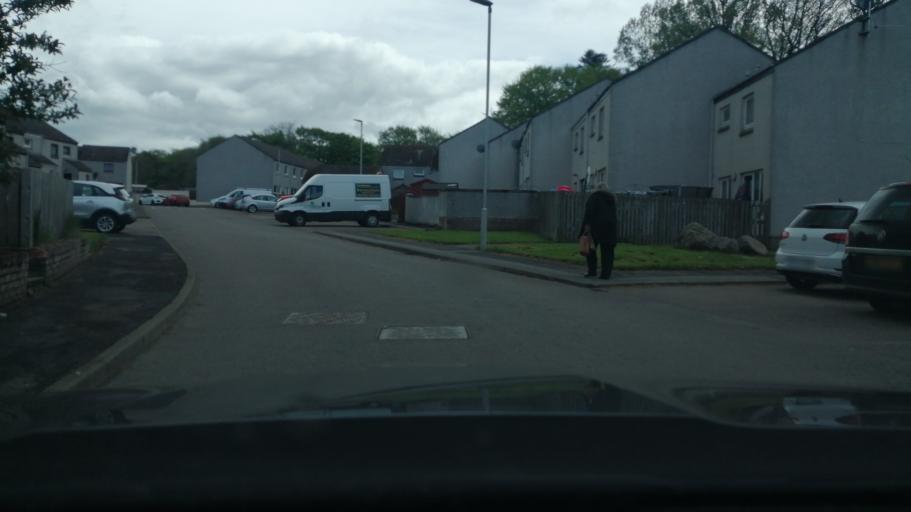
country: GB
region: Scotland
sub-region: Moray
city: Keith
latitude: 57.5350
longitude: -2.9443
